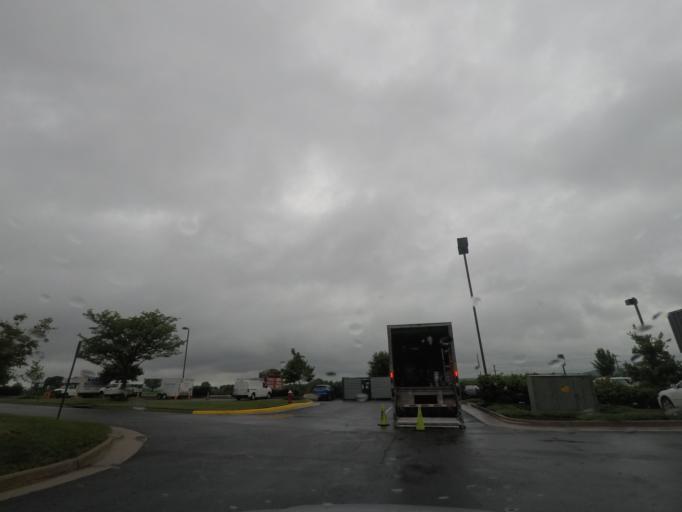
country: US
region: Virginia
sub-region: Loudoun County
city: Leesburg
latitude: 39.1130
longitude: -77.5367
